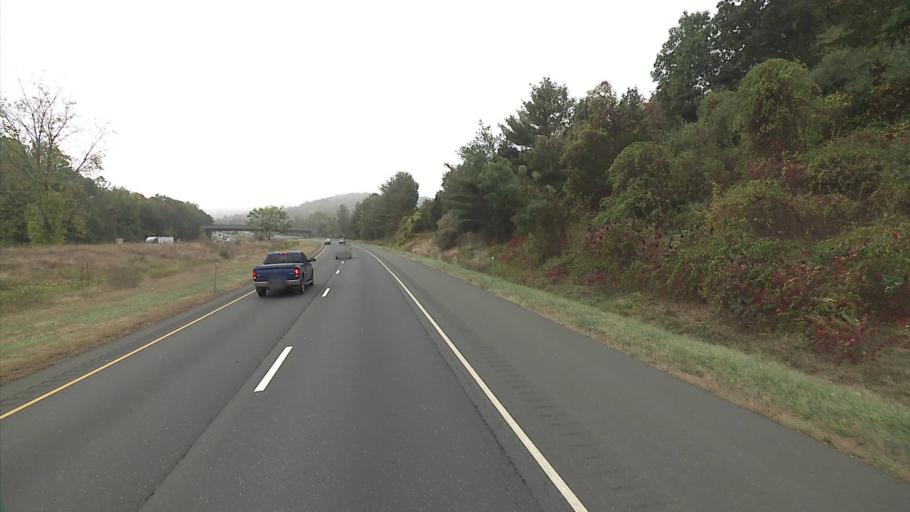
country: US
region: Connecticut
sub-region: New Haven County
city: Heritage Village
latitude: 41.4456
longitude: -73.2502
